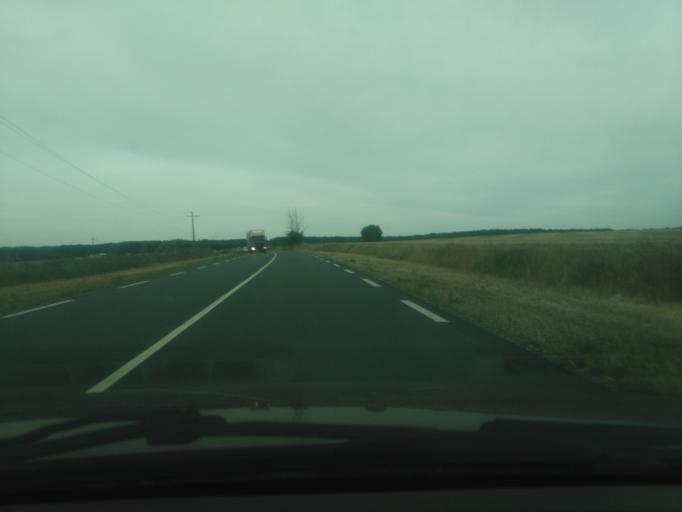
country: FR
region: Poitou-Charentes
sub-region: Departement de la Vienne
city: Chauvigny
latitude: 46.5640
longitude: 0.6565
